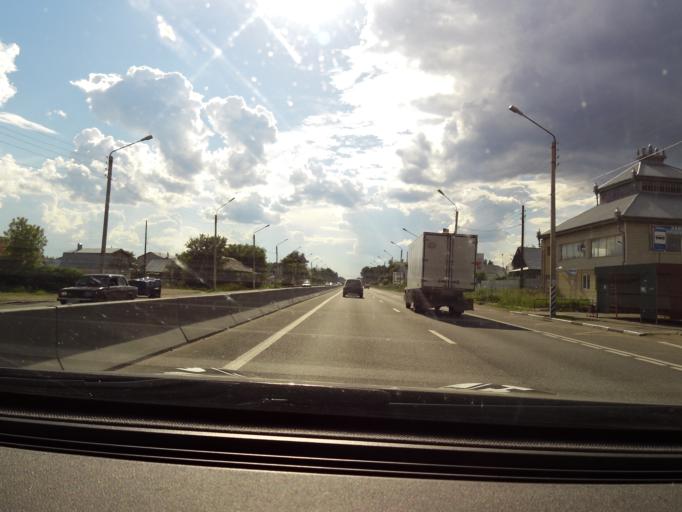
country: RU
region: Nizjnij Novgorod
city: Babino
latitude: 56.3025
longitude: 43.5753
